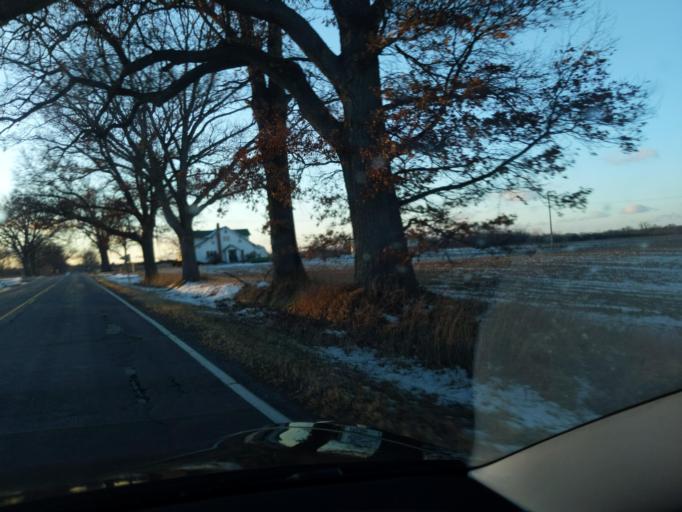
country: US
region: Michigan
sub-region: Ingham County
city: Stockbridge
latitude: 42.4467
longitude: -84.2132
